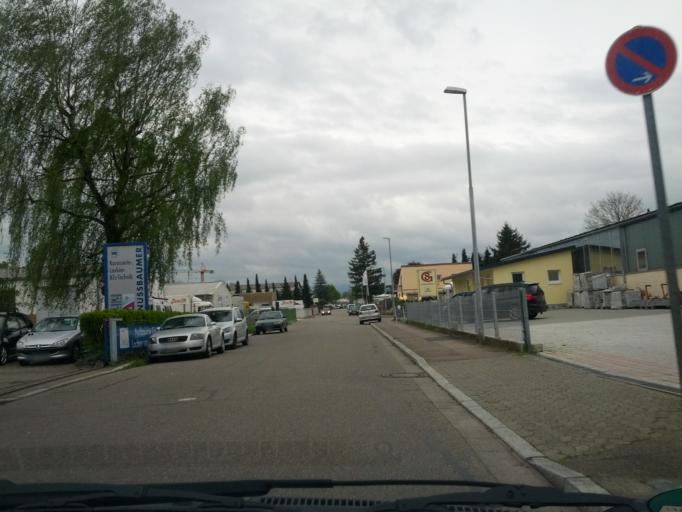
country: DE
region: Baden-Wuerttemberg
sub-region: Freiburg Region
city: Merdingen
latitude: 47.9987
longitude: 7.7189
